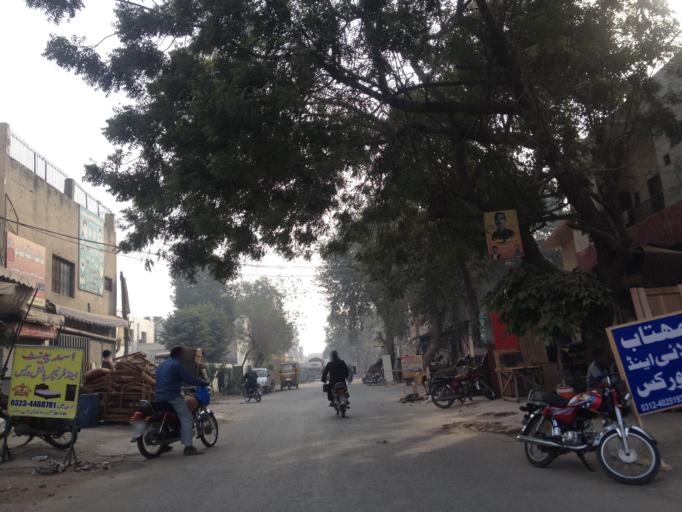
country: PK
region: Punjab
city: Lahore
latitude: 31.4654
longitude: 74.3084
